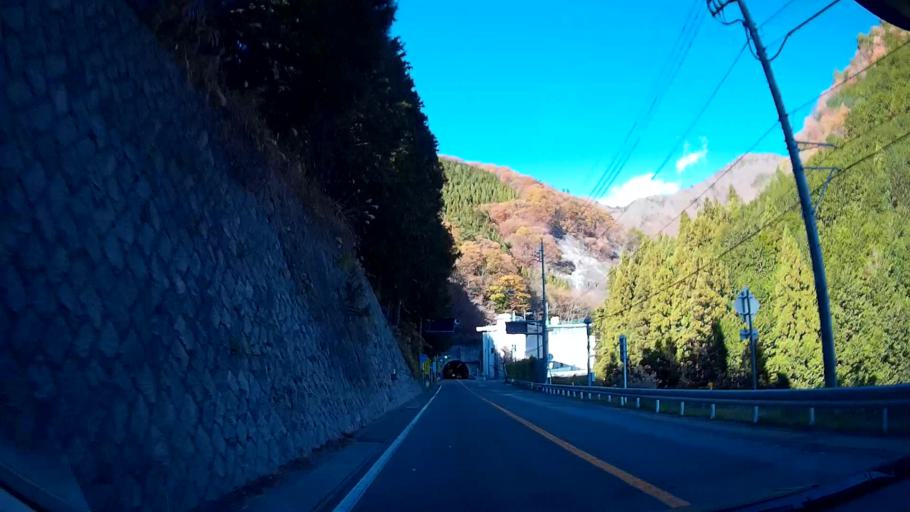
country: JP
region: Yamanashi
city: Enzan
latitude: 35.6064
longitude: 138.8041
